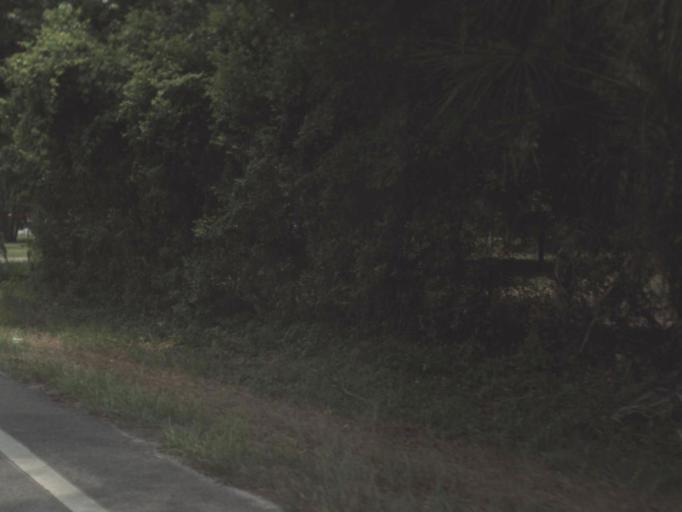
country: US
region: Florida
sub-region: Levy County
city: Chiefland
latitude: 29.4747
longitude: -82.8732
